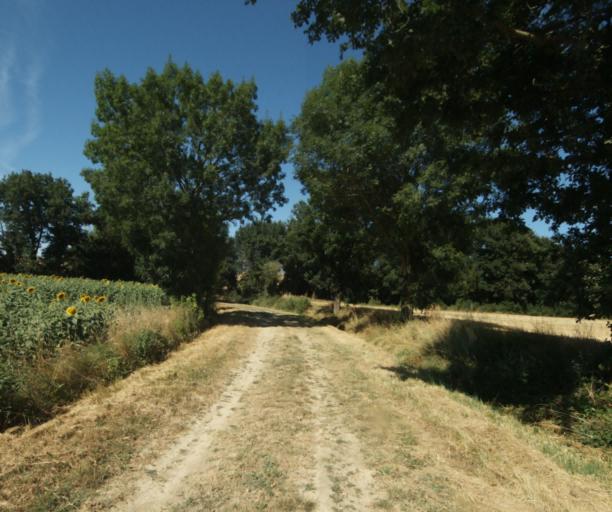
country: FR
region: Midi-Pyrenees
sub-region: Departement de la Haute-Garonne
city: Saint-Felix-Lauragais
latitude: 43.4975
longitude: 1.9159
